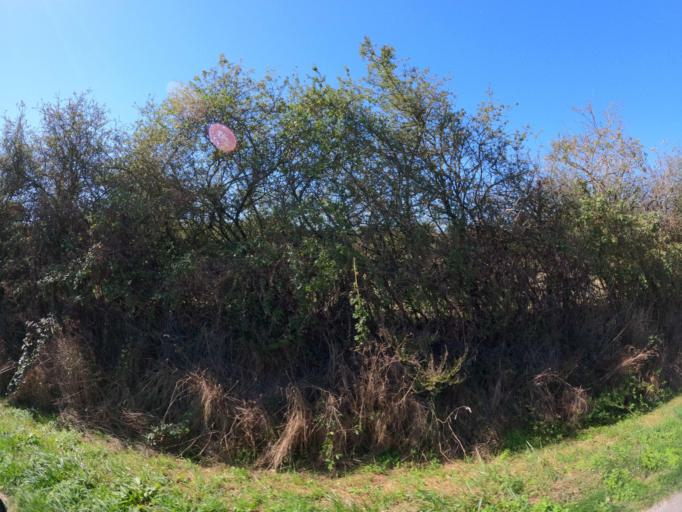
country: FR
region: Poitou-Charentes
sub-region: Departement de la Vienne
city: Lathus-Saint-Remy
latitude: 46.2860
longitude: 1.0075
